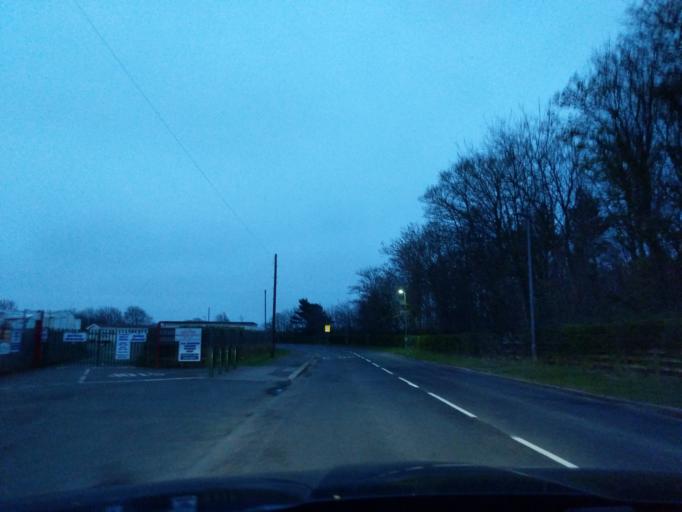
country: GB
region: England
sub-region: Northumberland
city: Cresswell
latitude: 55.2155
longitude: -1.5509
